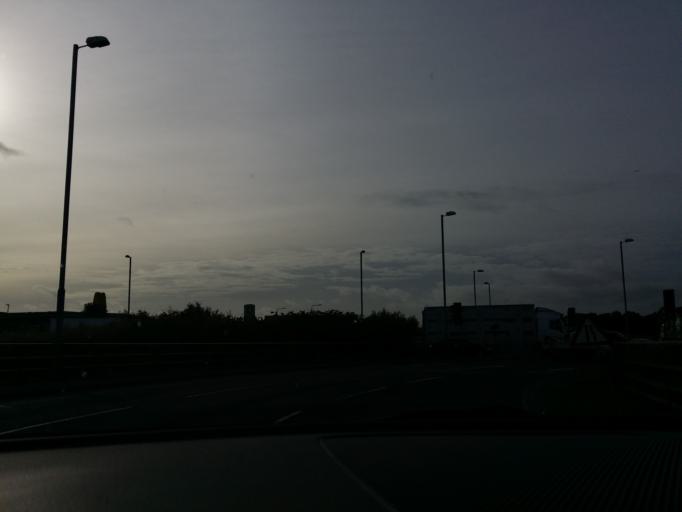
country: GB
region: Scotland
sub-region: Edinburgh
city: Newbridge
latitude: 55.9388
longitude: -3.4015
